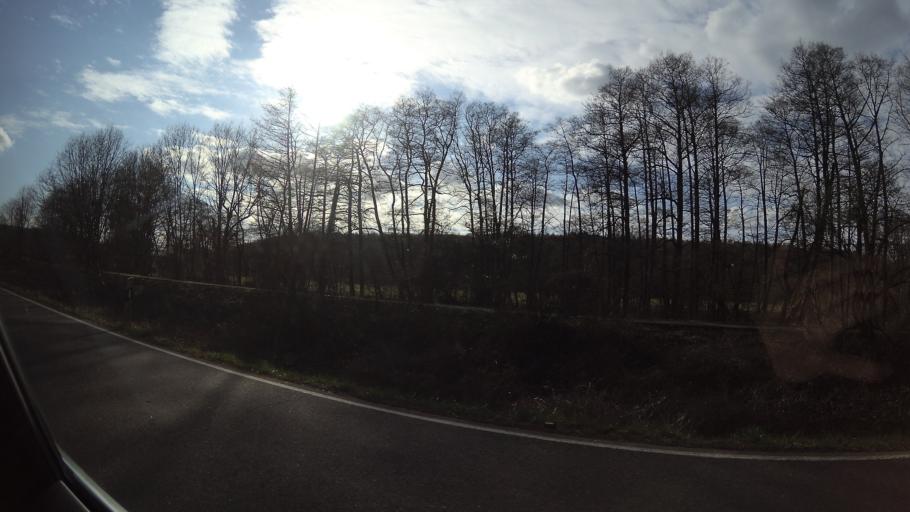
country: DE
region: Saarland
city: Blieskastel
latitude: 49.1880
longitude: 7.2499
